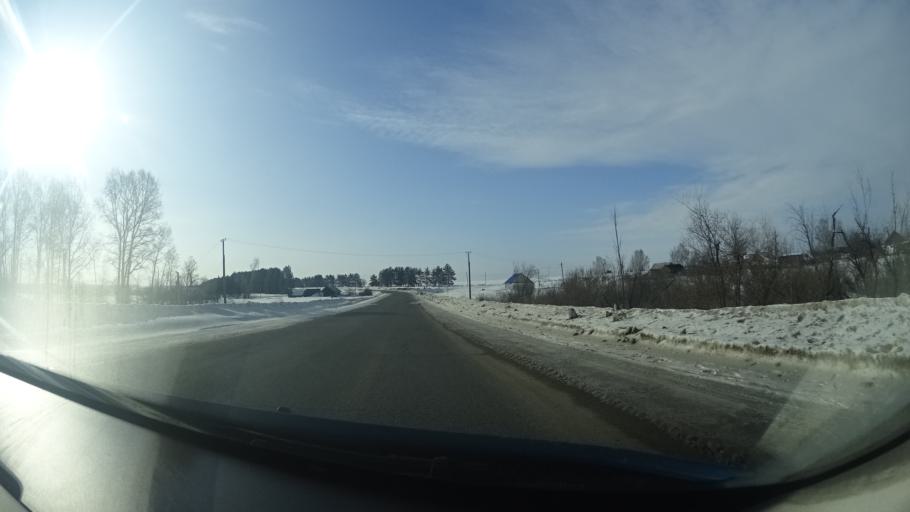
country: RU
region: Perm
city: Kuyeda
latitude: 56.4730
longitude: 55.5889
